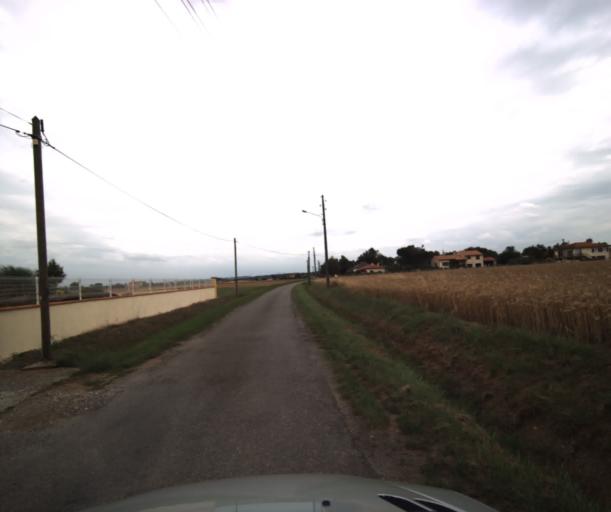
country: FR
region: Midi-Pyrenees
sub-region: Departement de la Haute-Garonne
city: Labarthe-sur-Leze
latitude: 43.4560
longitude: 1.3802
